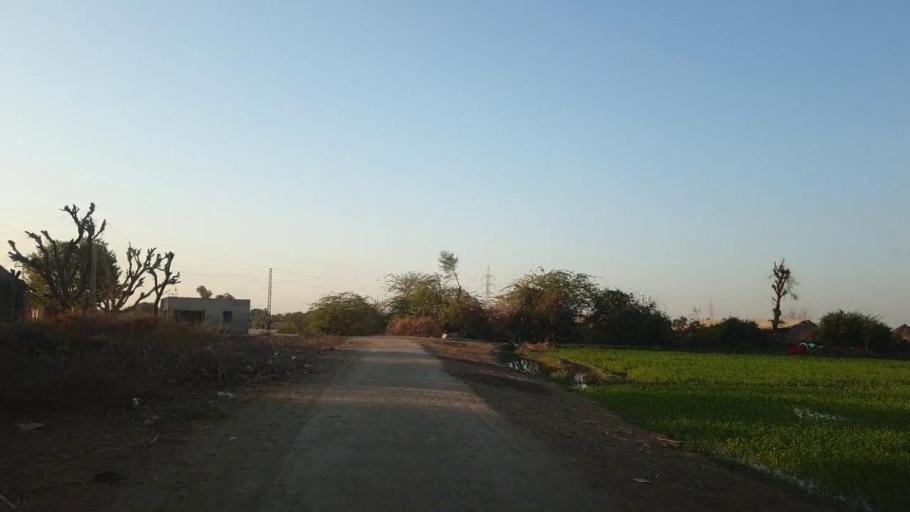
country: PK
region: Sindh
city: Mirpur Khas
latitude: 25.7032
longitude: 69.0419
